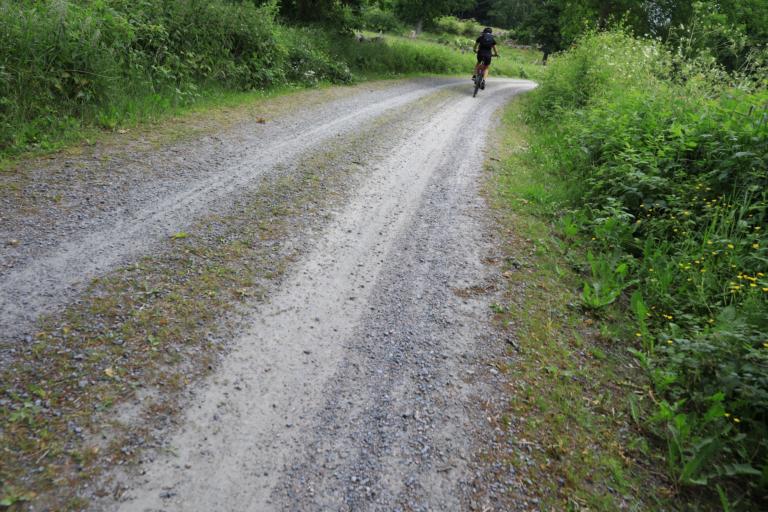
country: SE
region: Halland
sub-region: Varbergs Kommun
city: Varberg
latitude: 57.1712
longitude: 12.2744
